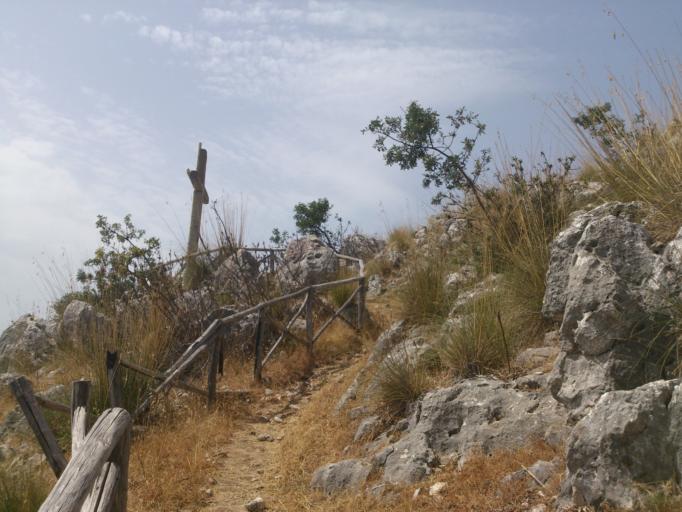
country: IT
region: Calabria
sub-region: Provincia di Reggio Calabria
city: Stilo
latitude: 38.4802
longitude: 16.4653
